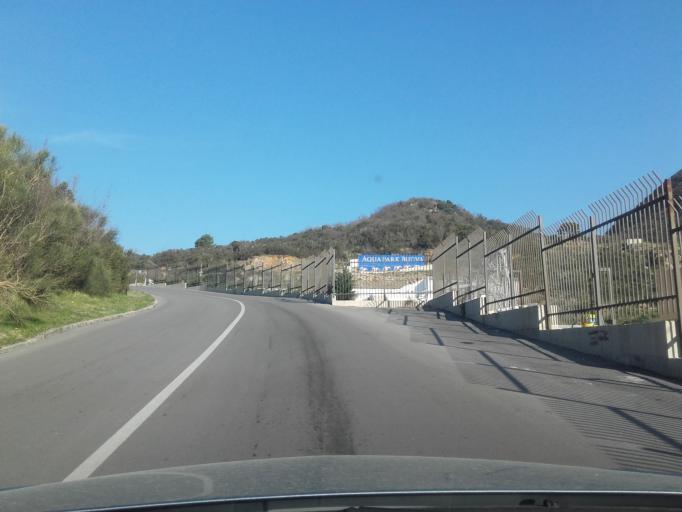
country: ME
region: Budva
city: Budva
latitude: 42.2924
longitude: 18.8218
